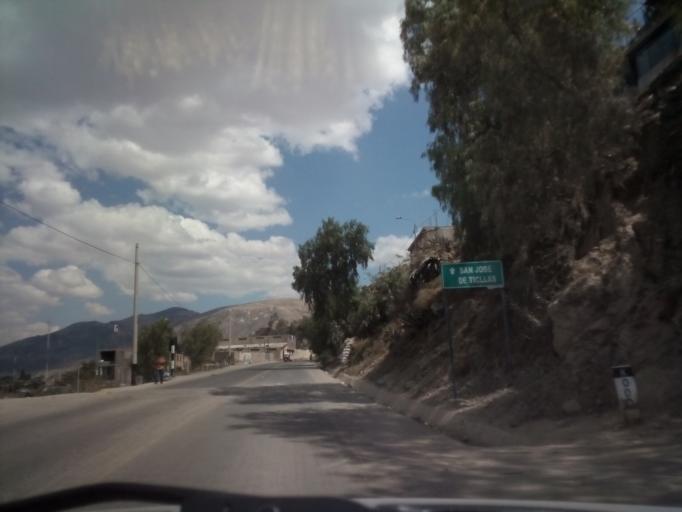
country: PE
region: Ayacucho
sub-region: Provincia de Huamanga
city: Ayacucho
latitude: -13.1517
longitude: -74.2334
